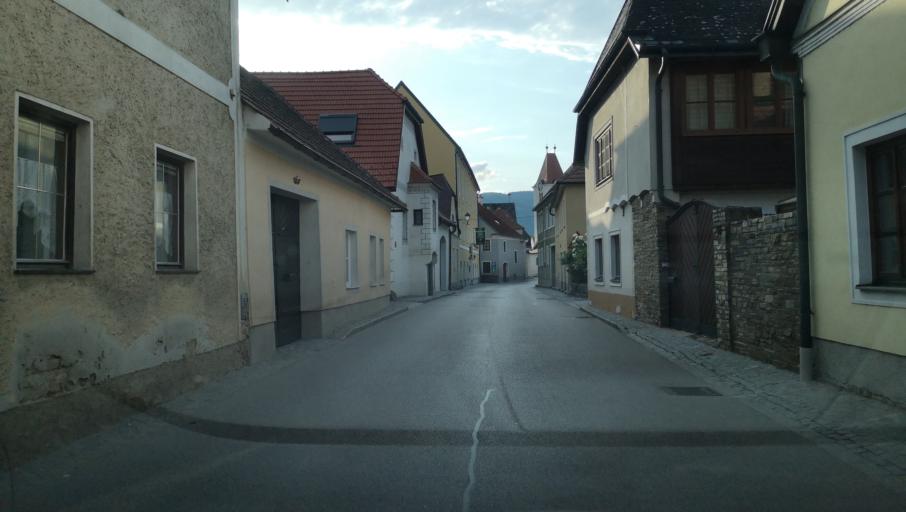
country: AT
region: Lower Austria
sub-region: Politischer Bezirk Krems
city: Durnstein
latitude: 48.3954
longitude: 15.5063
